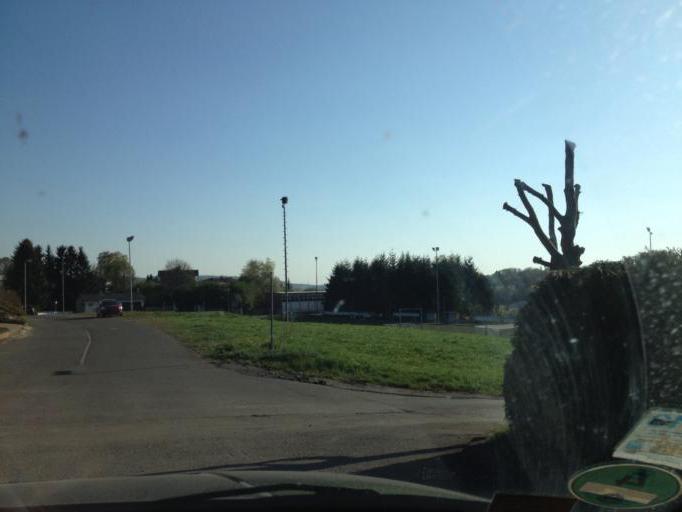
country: DE
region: Saarland
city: Sankt Wendel
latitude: 49.4794
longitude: 7.1813
